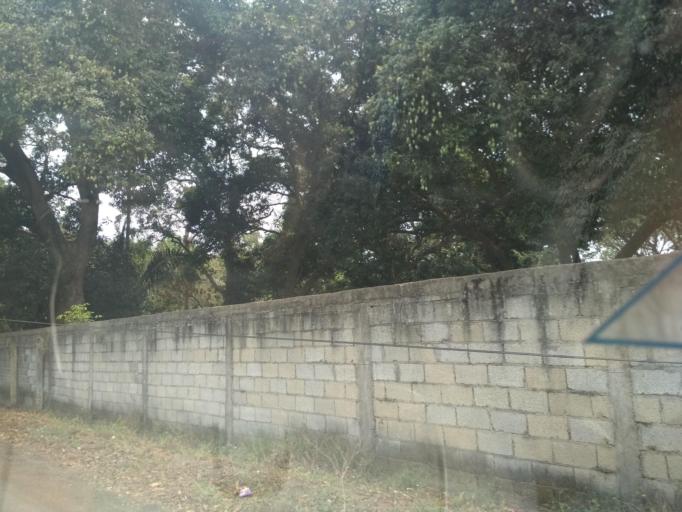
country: MX
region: Veracruz
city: El Tejar
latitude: 19.0523
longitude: -96.1537
